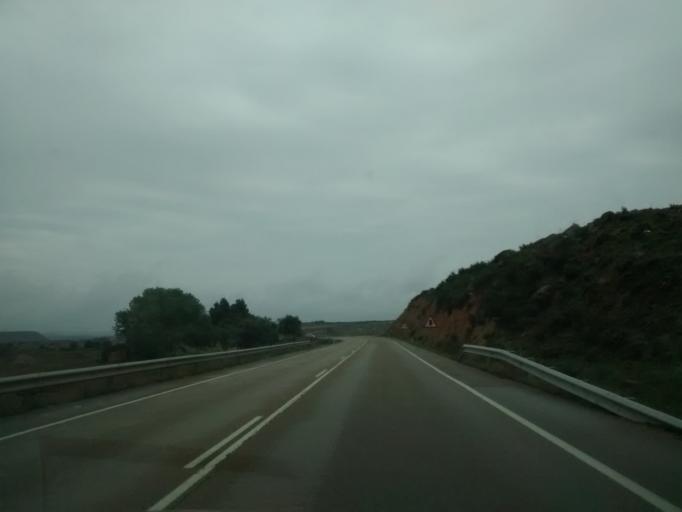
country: ES
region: Aragon
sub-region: Provincia de Zaragoza
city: Caspe
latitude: 41.2154
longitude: -0.0100
